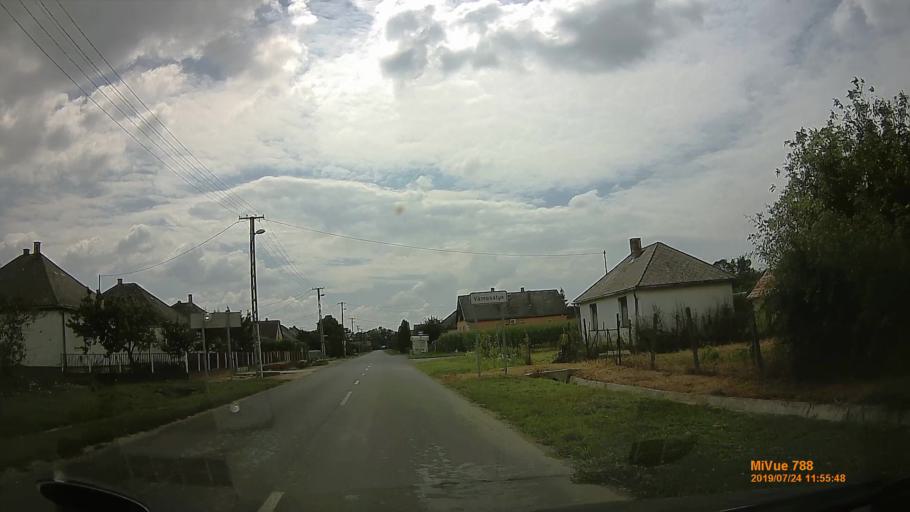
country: HU
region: Szabolcs-Szatmar-Bereg
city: Vasarosnameny
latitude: 48.2055
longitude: 22.4137
